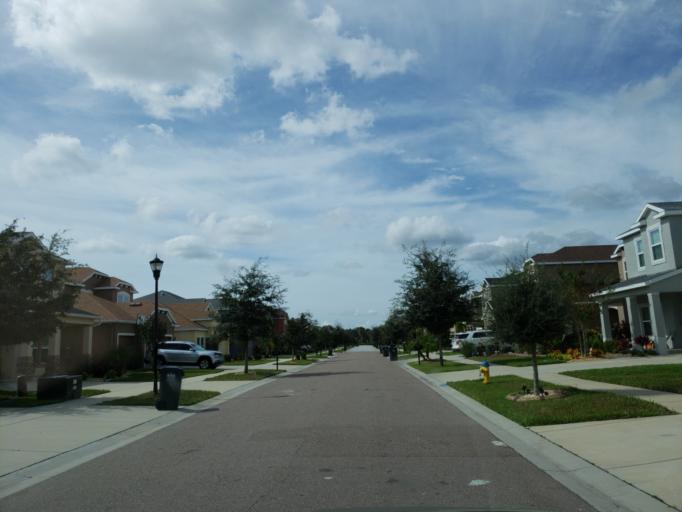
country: US
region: Florida
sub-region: Hillsborough County
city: Riverview
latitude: 27.8531
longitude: -82.3304
